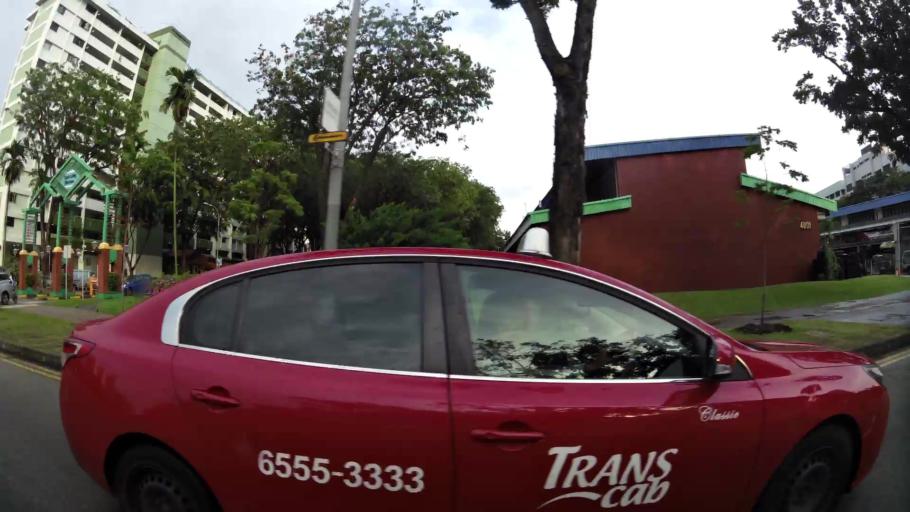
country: SG
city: Singapore
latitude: 1.3620
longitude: 103.8559
